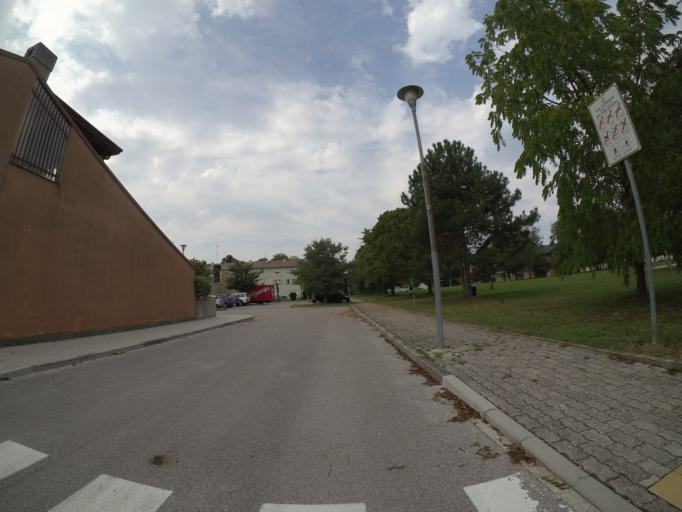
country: IT
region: Friuli Venezia Giulia
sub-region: Provincia di Udine
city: Codroipo
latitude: 45.9559
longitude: 12.9976
